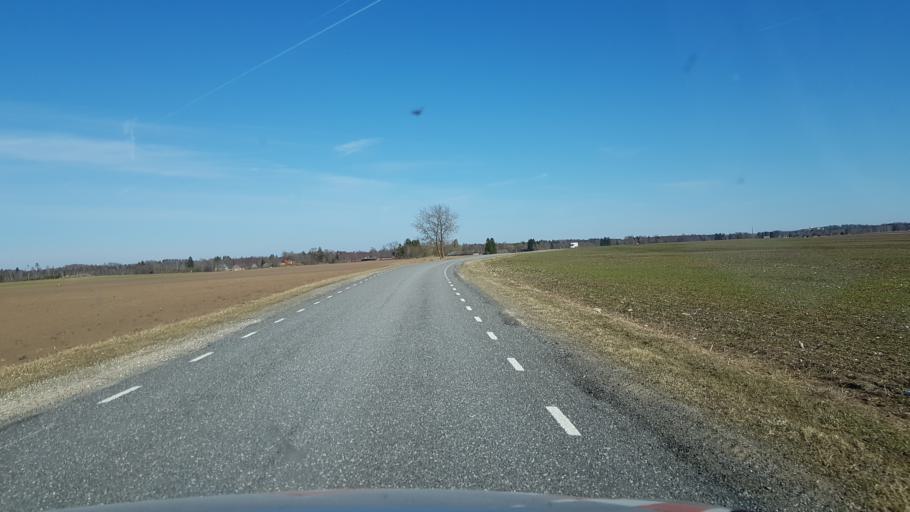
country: EE
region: Laeaene-Virumaa
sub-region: Rakke vald
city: Rakke
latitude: 59.0078
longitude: 26.1700
